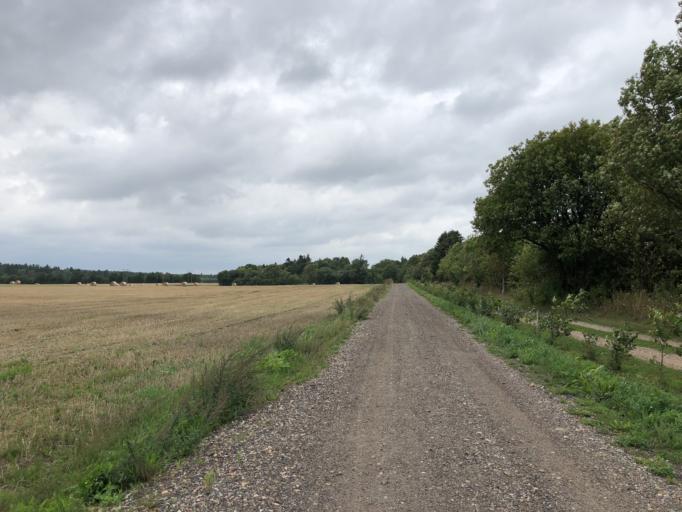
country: DK
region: Central Jutland
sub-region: Herning Kommune
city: Lind
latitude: 56.0639
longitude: 8.9852
